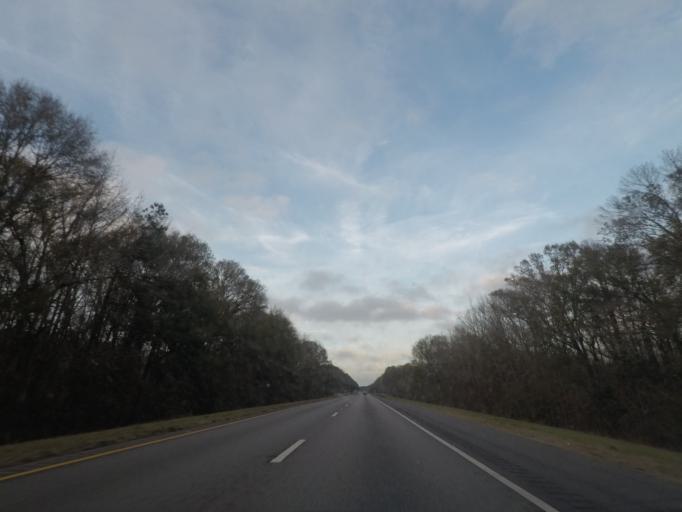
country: US
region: South Carolina
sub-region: Orangeburg County
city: Holly Hill
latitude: 33.3430
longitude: -80.5337
